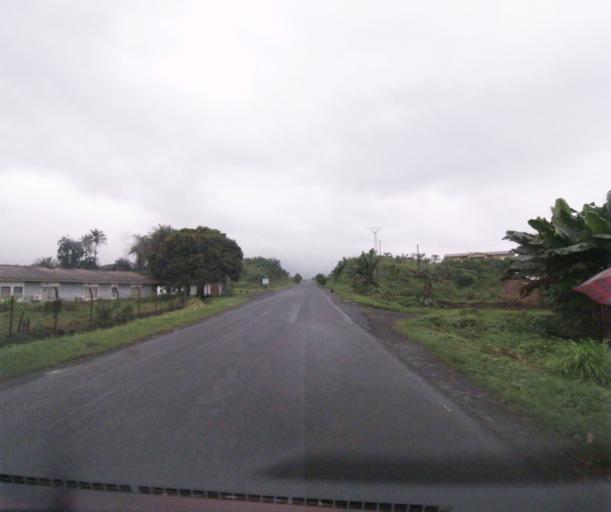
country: CM
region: South-West Province
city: Idenao
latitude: 4.2086
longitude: 8.9931
